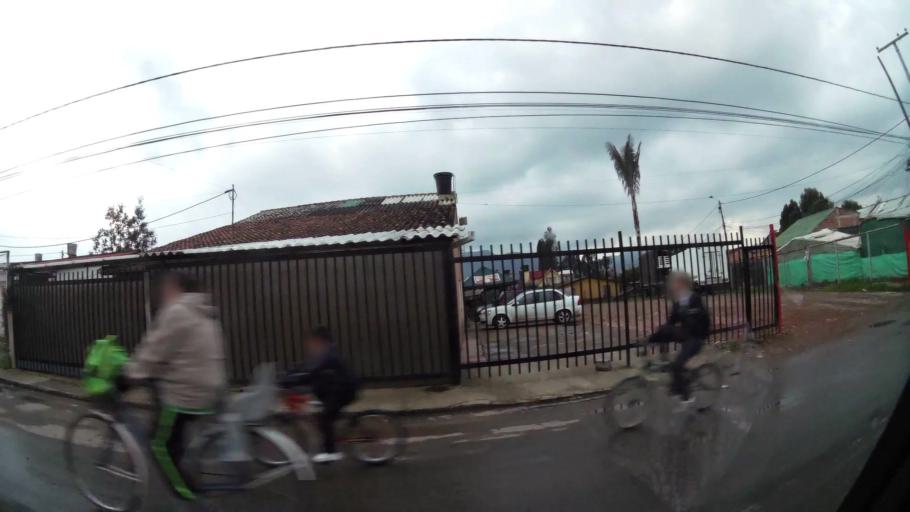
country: CO
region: Cundinamarca
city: Chia
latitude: 4.8400
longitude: -74.0598
